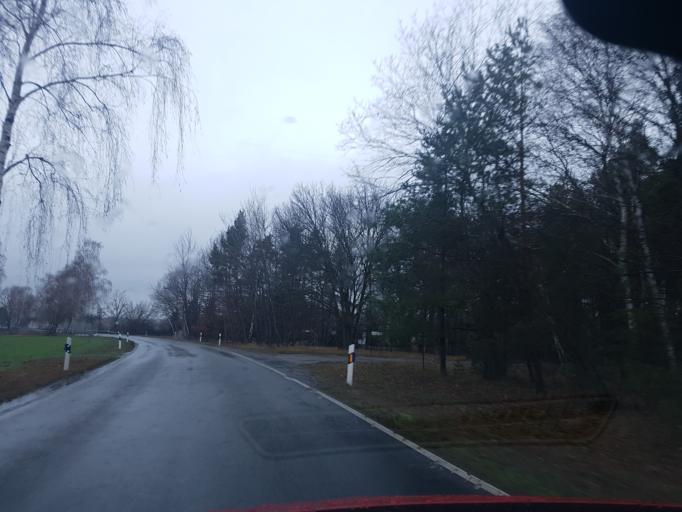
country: DE
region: Brandenburg
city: Schilda
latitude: 51.6239
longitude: 13.3186
